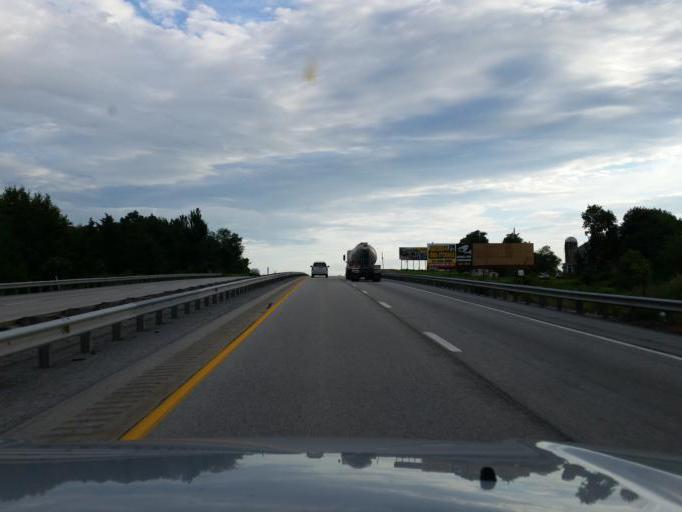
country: US
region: Pennsylvania
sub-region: Adams County
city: Lake Meade
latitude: 40.0240
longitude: -77.0899
